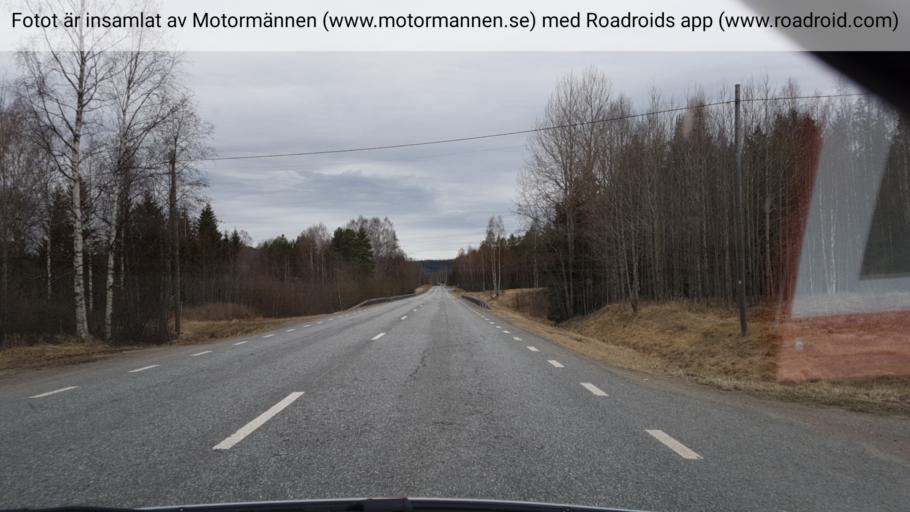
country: SE
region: Vaesternorrland
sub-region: Solleftea Kommun
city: Solleftea
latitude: 63.2642
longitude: 17.2139
